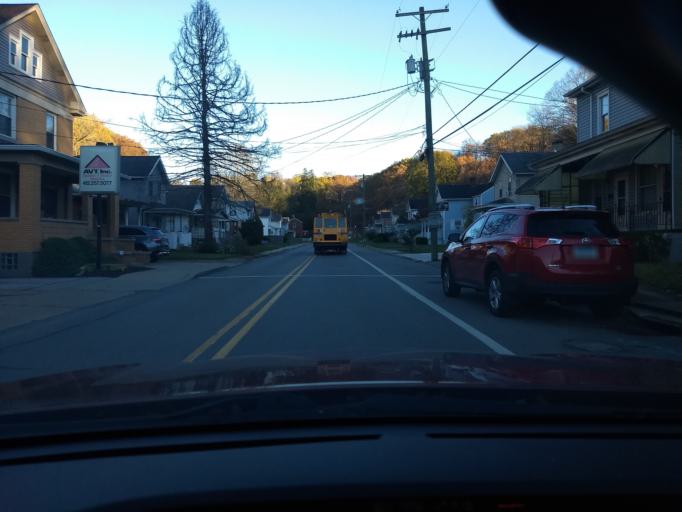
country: US
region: Pennsylvania
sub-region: Allegheny County
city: Bridgeville
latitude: 40.3545
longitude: -80.1040
